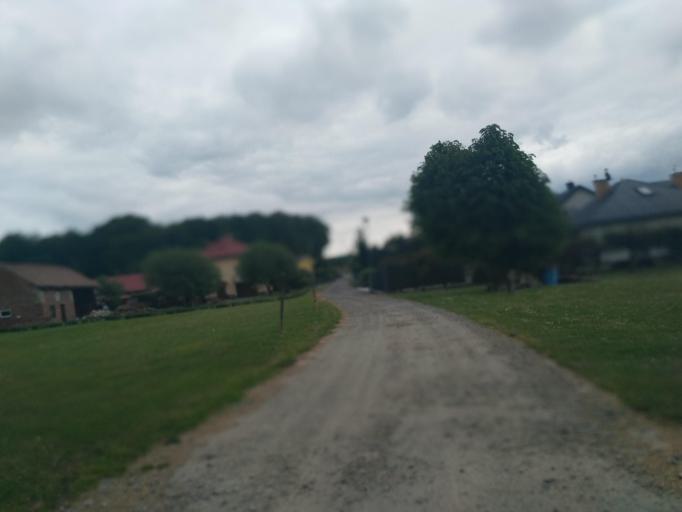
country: PL
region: Subcarpathian Voivodeship
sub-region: Powiat krosnienski
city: Odrzykon
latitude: 49.7251
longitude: 21.7046
